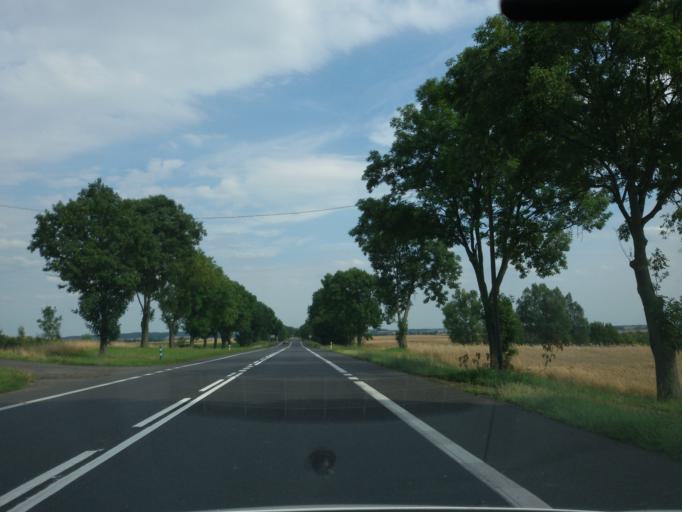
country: PL
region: Lower Silesian Voivodeship
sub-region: Powiat polkowicki
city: Gaworzyce
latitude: 51.6335
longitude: 15.8983
